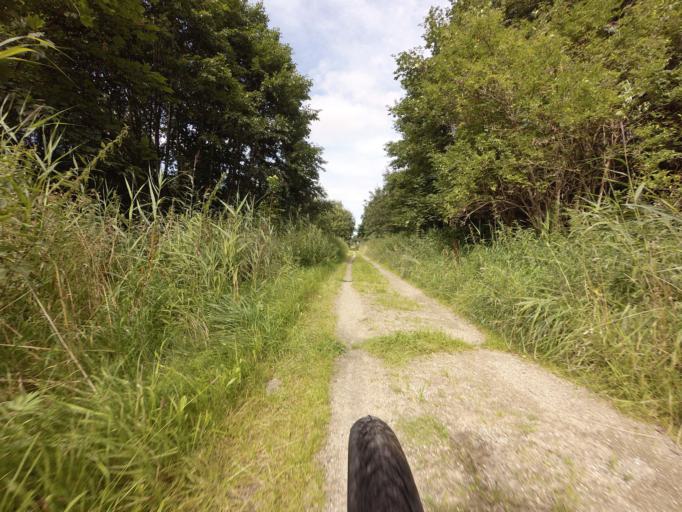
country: DK
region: Central Jutland
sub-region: Syddjurs Kommune
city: Ryomgard
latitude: 56.3877
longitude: 10.5330
